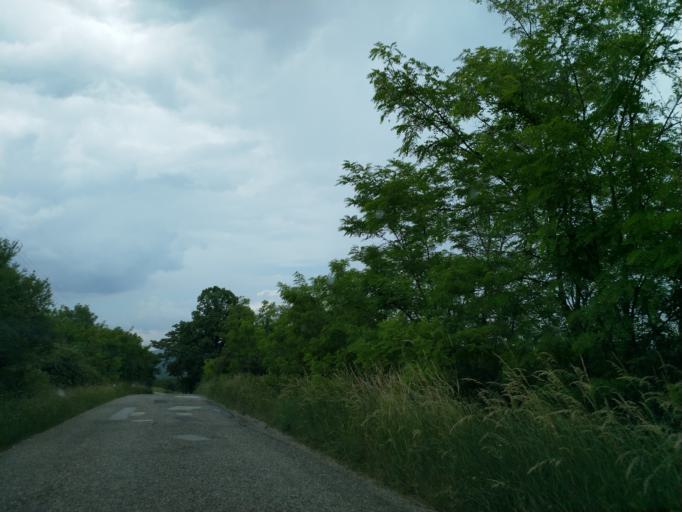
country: RS
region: Central Serbia
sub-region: Borski Okrug
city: Bor
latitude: 43.9917
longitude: 21.9767
